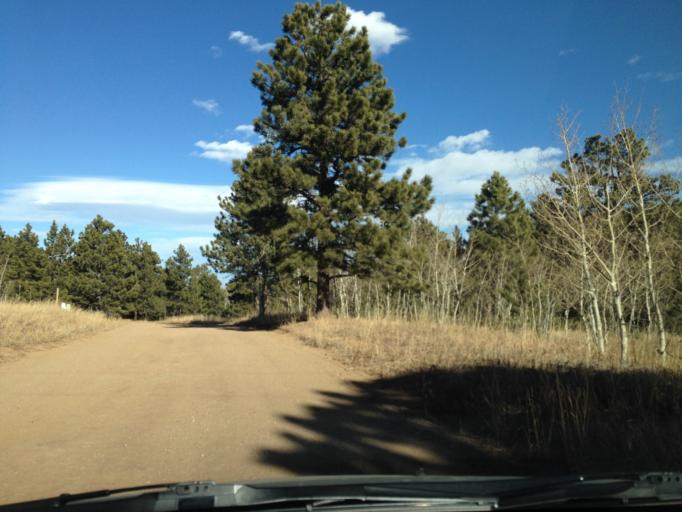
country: US
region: Colorado
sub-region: Boulder County
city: Coal Creek
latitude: 39.9141
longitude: -105.3536
